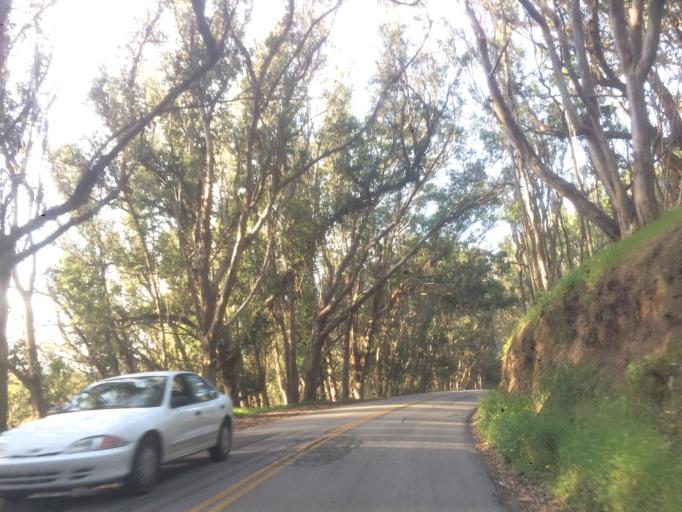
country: US
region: California
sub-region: San Luis Obispo County
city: Los Osos
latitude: 35.2858
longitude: -120.8801
